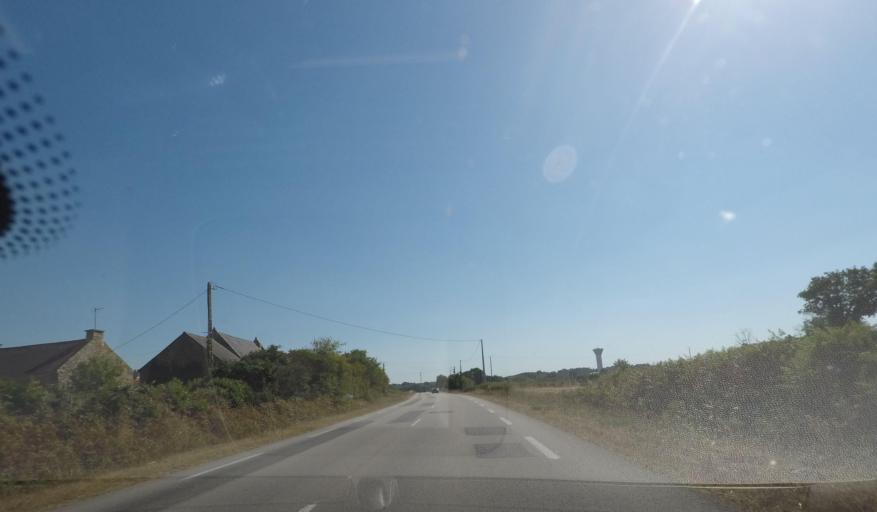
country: FR
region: Brittany
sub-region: Departement du Morbihan
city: Peaule
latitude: 47.5474
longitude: -2.3982
